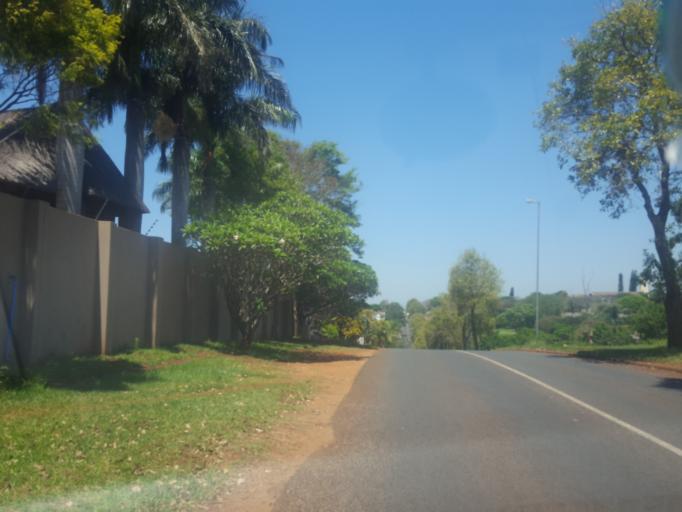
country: ZA
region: KwaZulu-Natal
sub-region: uThungulu District Municipality
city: Empangeni
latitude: -28.7497
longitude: 31.9022
